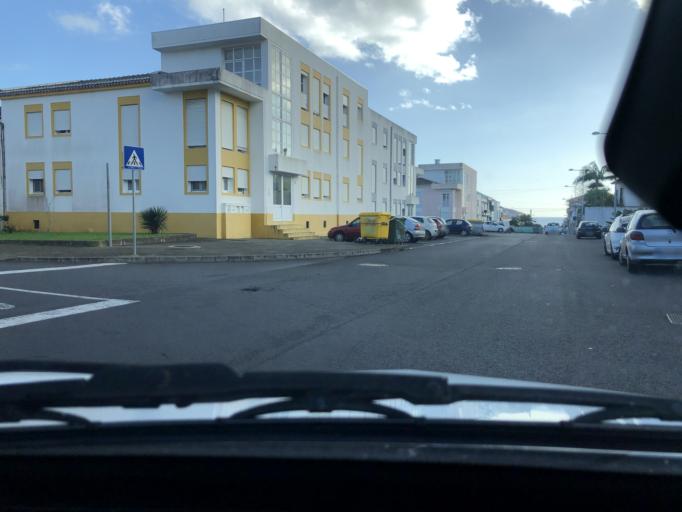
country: PT
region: Azores
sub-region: Ponta Delgada
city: Rosto de Cao
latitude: 37.7464
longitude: -25.6543
